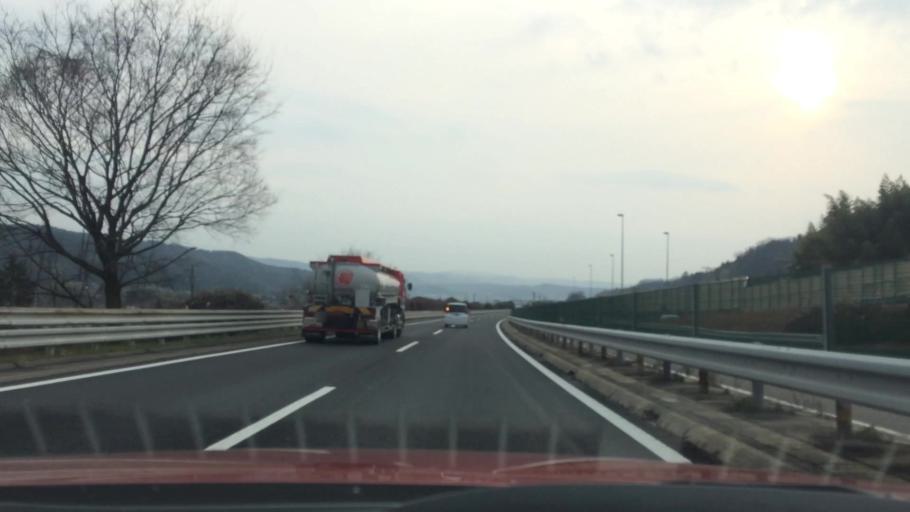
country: JP
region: Gifu
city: Mizunami
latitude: 35.3954
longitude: 137.2756
